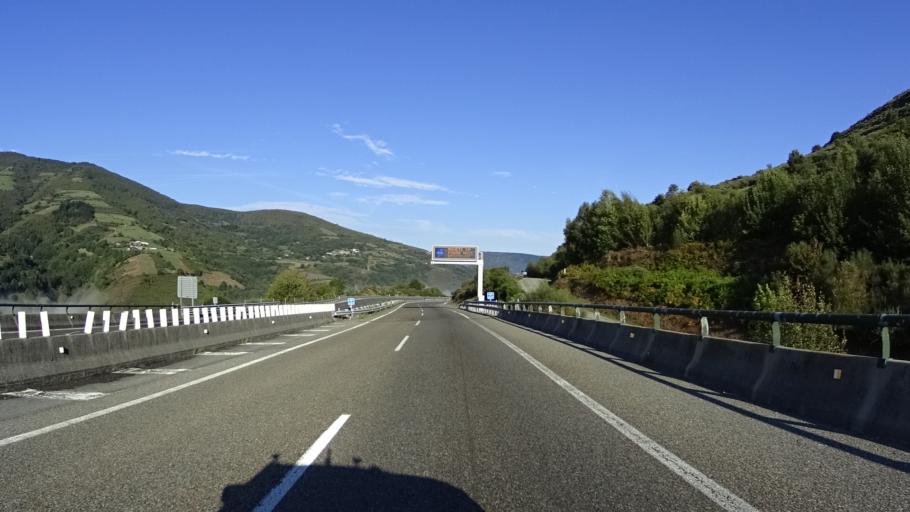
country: ES
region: Galicia
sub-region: Provincia de Lugo
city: San Roman
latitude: 42.7544
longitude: -7.0692
